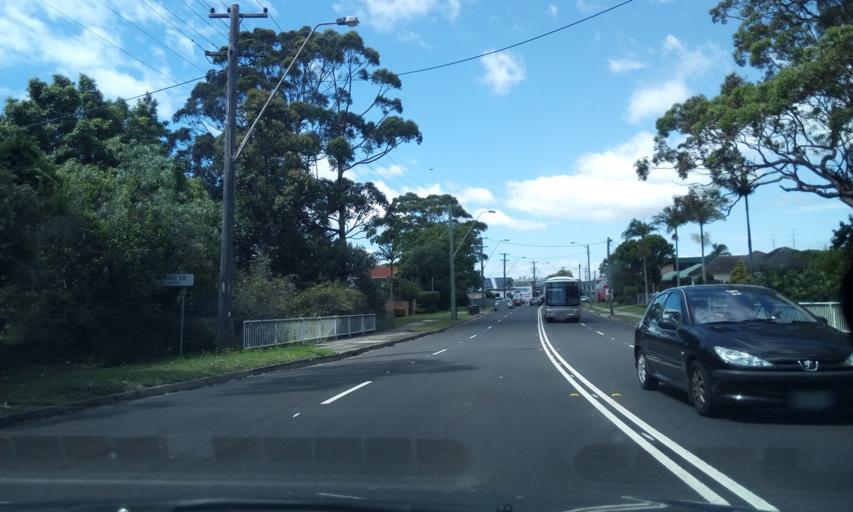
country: AU
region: New South Wales
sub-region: Wollongong
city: Corrimal
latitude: -34.3796
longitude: 150.8966
